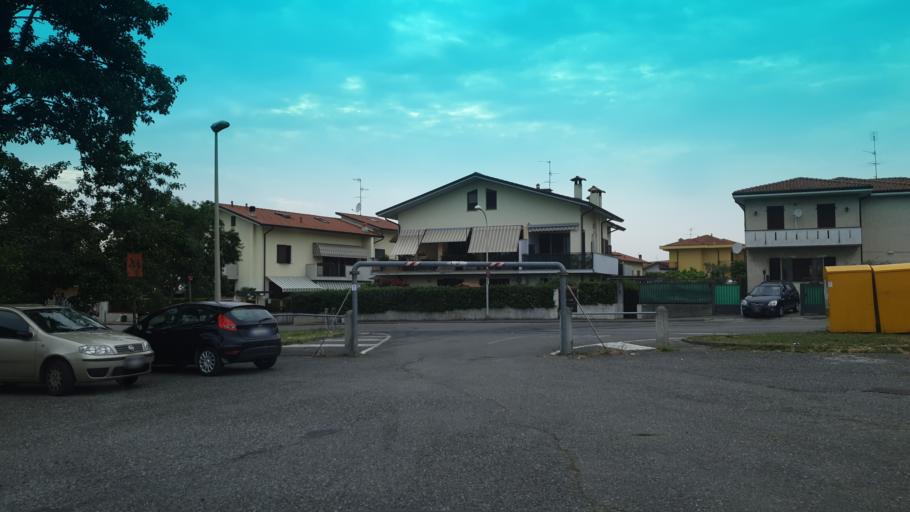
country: IT
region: Lombardy
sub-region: Provincia di Bergamo
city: Fara Gera d'Adda
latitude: 45.5494
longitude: 9.5350
